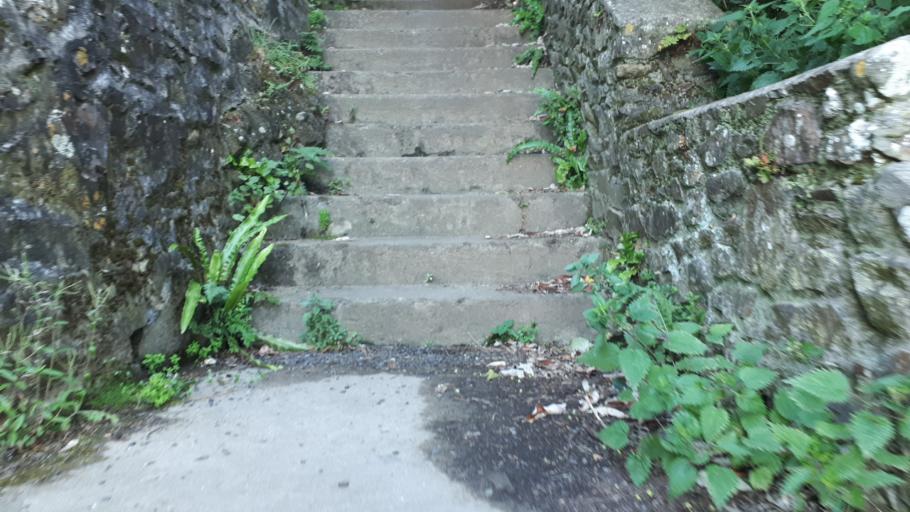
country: FR
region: Brittany
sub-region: Departement des Cotes-d'Armor
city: Etables-sur-Mer
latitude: 48.6274
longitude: -2.8222
